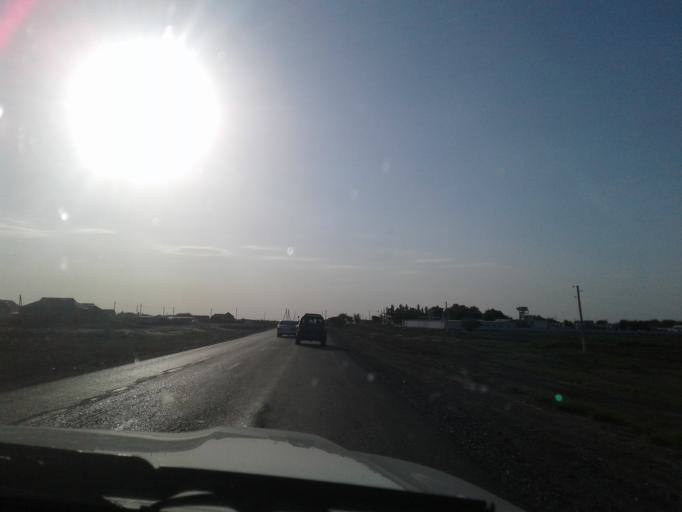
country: TM
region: Mary
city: Yoloeten
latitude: 37.3491
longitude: 62.2581
